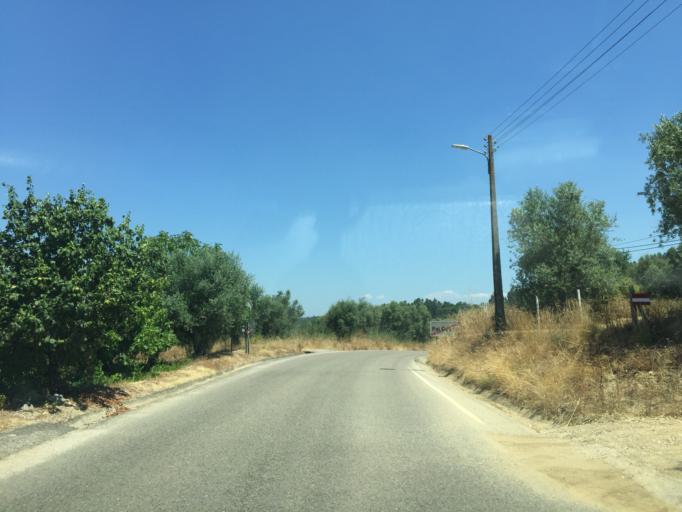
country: PT
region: Santarem
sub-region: Tomar
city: Tomar
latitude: 39.5887
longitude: -8.3281
